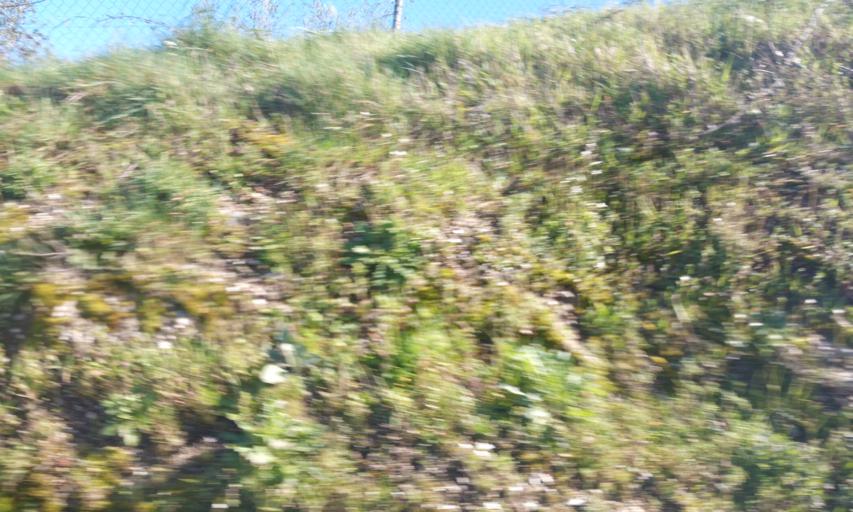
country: PT
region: Guarda
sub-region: Seia
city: Seia
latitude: 40.4685
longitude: -7.6222
